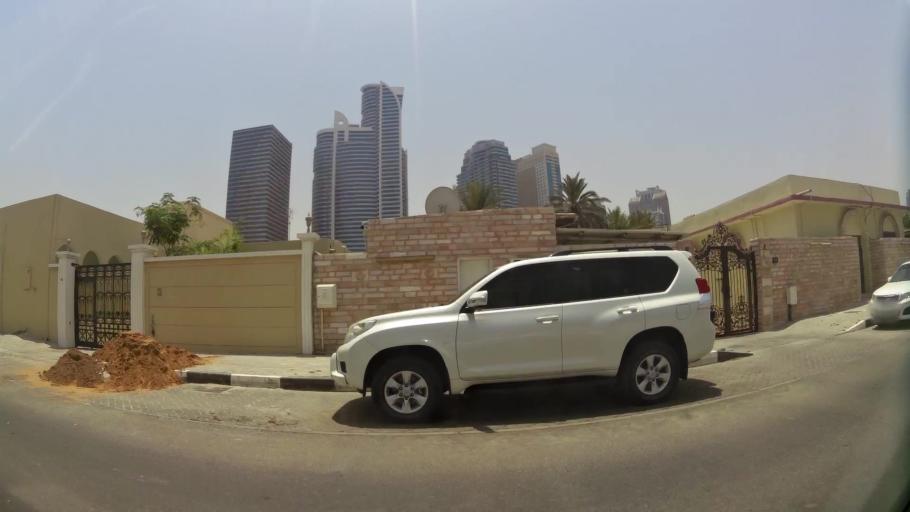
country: AE
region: Ash Shariqah
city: Sharjah
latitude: 25.3376
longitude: 55.3719
